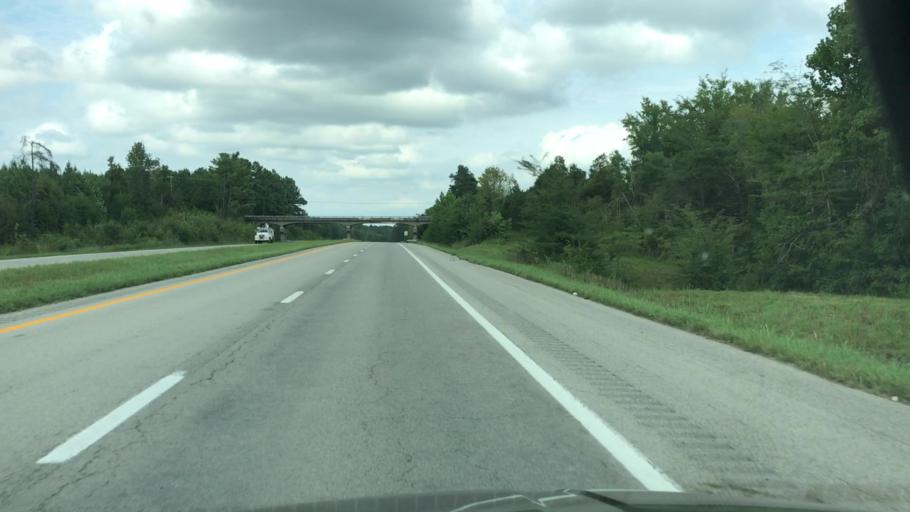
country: US
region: Kentucky
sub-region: Caldwell County
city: Princeton
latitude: 37.1460
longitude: -87.8012
